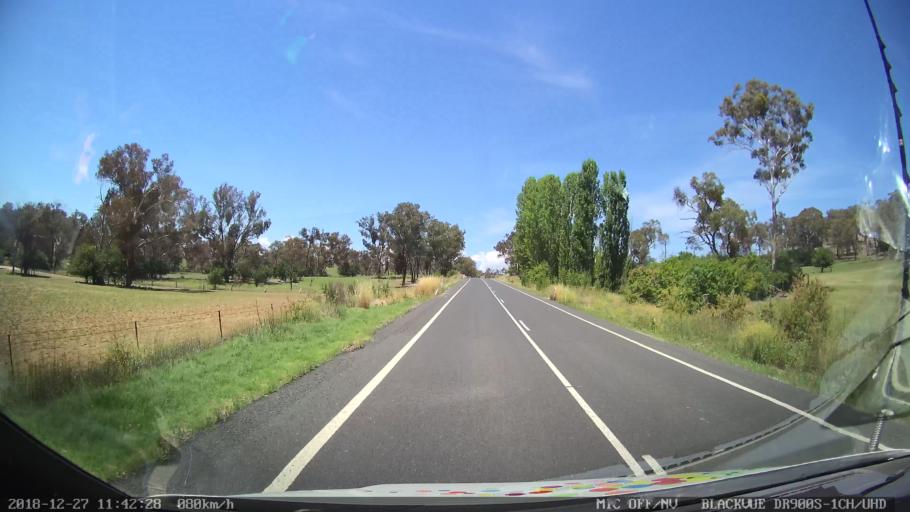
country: AU
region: New South Wales
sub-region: Bathurst Regional
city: Perthville
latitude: -33.5489
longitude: 149.4784
